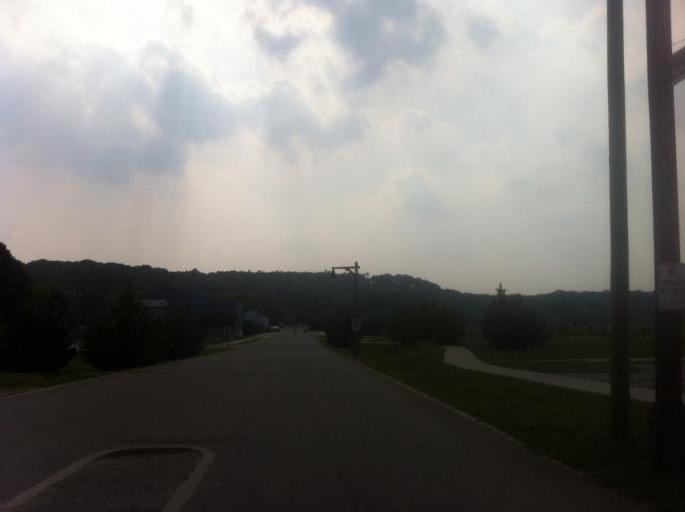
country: US
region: New York
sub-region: Nassau County
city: Oyster Bay
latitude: 40.8757
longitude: -73.5361
